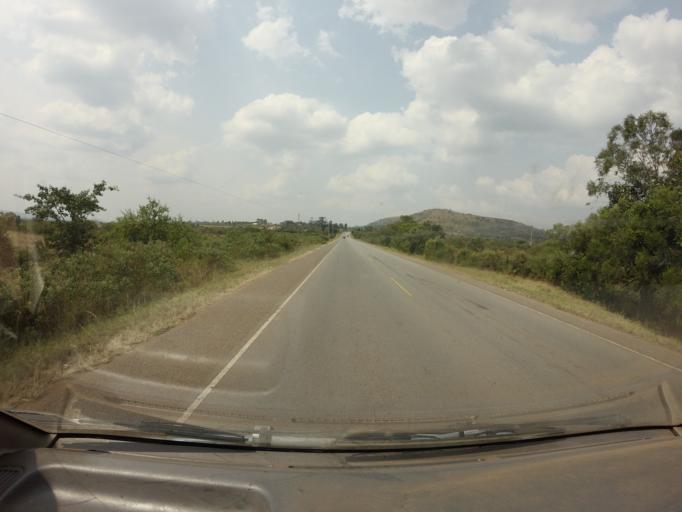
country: UG
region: Central Region
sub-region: Lyantonde District
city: Lyantonde
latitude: -0.3942
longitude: 31.1788
